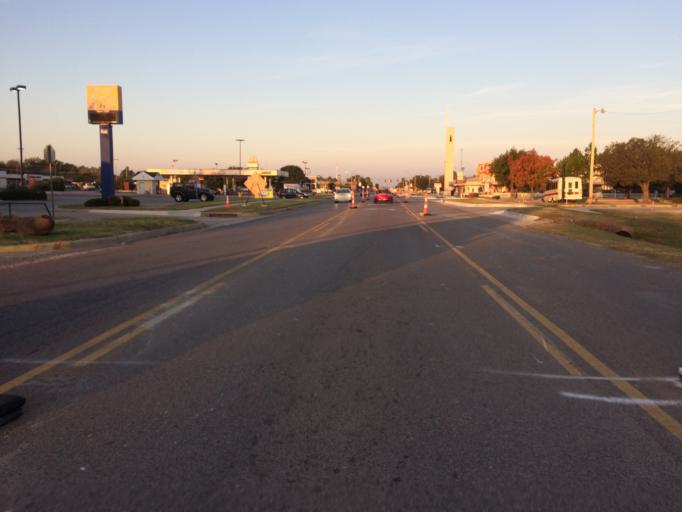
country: US
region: Oklahoma
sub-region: Cleveland County
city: Norman
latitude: 35.2039
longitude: -97.4645
